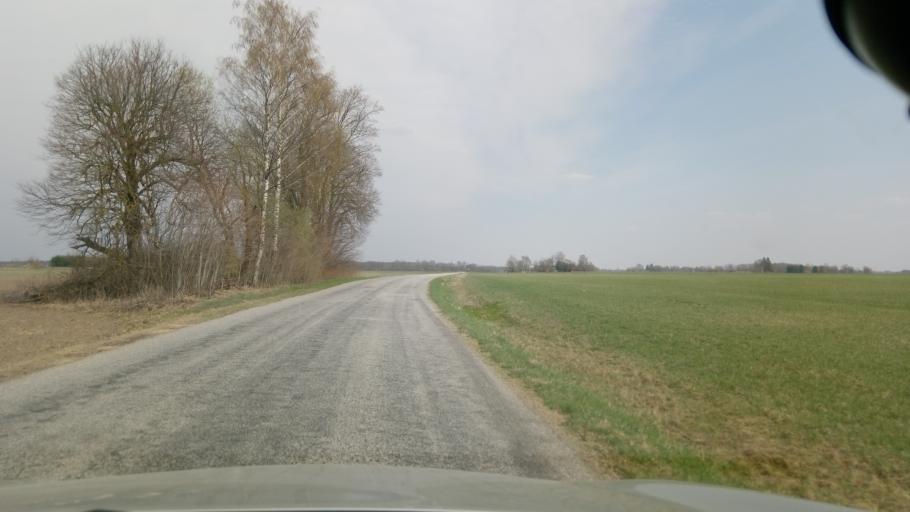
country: EE
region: Viljandimaa
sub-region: Vohma linn
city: Vohma
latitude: 58.6766
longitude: 25.5786
